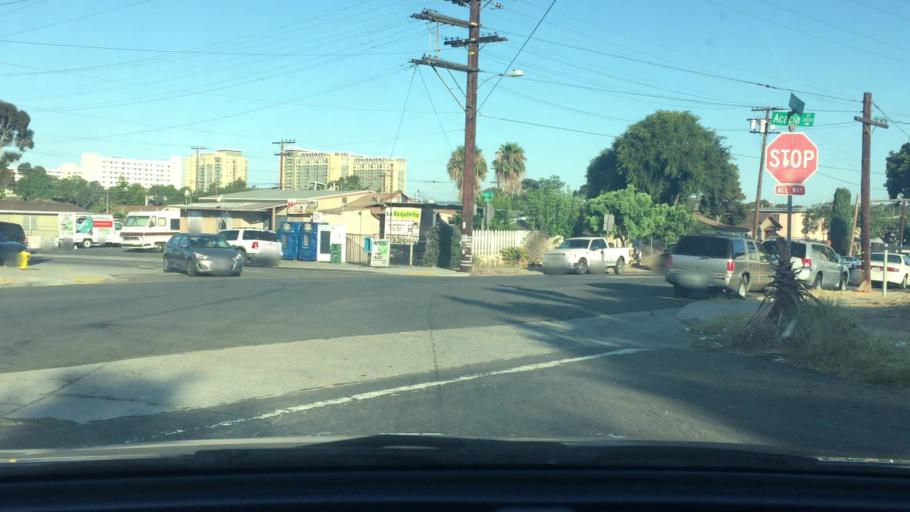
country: US
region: California
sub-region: San Diego County
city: National City
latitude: 32.6887
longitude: -117.1120
